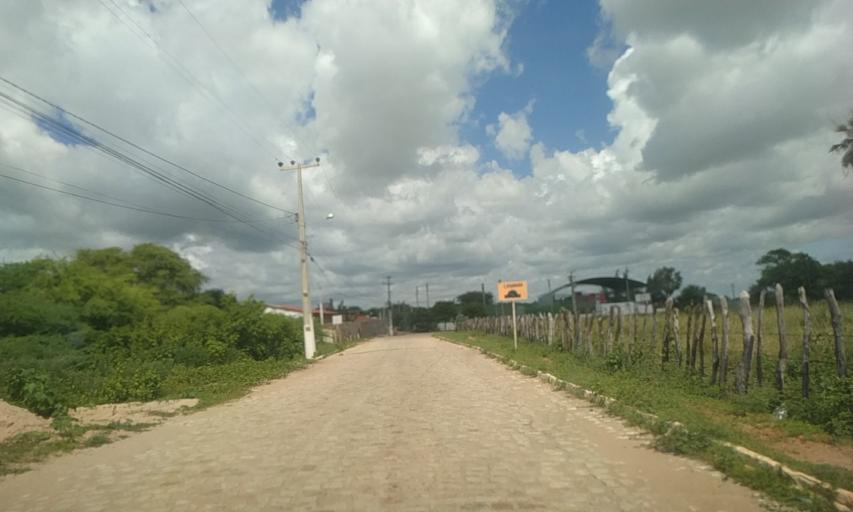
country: BR
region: Rio Grande do Norte
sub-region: Areia Branca
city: Areia Branca
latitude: -4.9316
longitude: -37.1102
